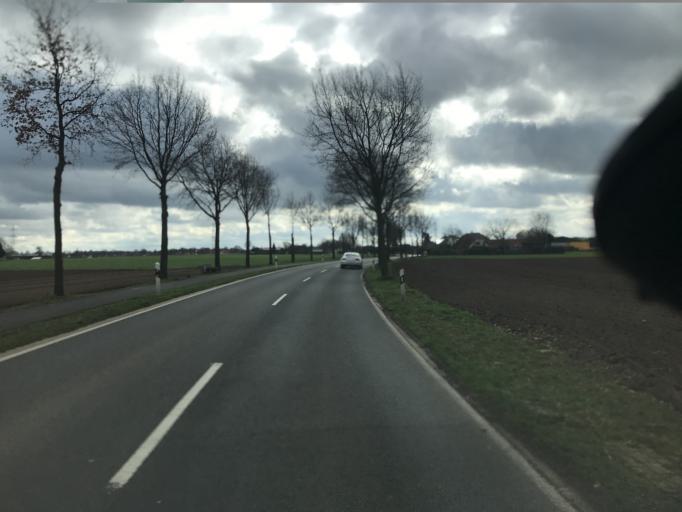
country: DE
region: North Rhine-Westphalia
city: Tonisvorst
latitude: 51.2675
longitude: 6.4585
